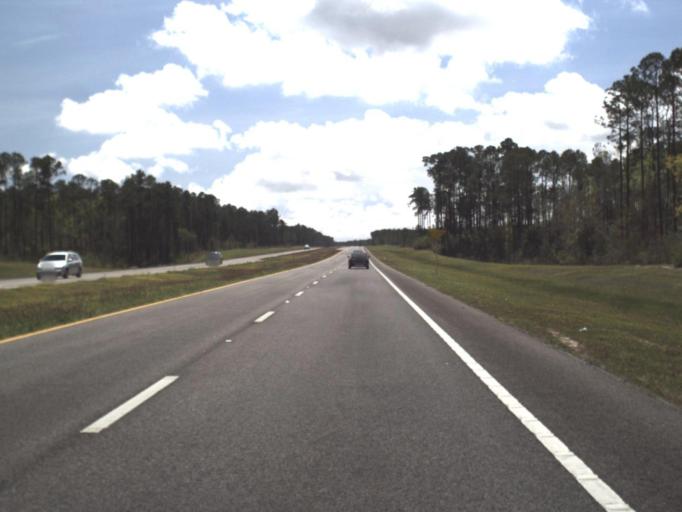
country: US
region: Florida
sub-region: Bay County
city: Laguna Beach
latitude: 30.4108
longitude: -85.8695
